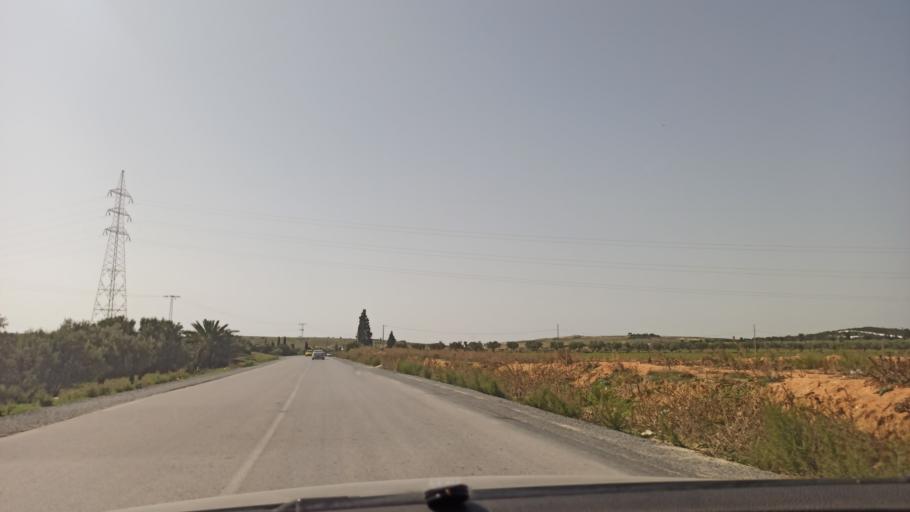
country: TN
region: Manouba
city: Manouba
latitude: 36.7481
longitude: 10.0974
